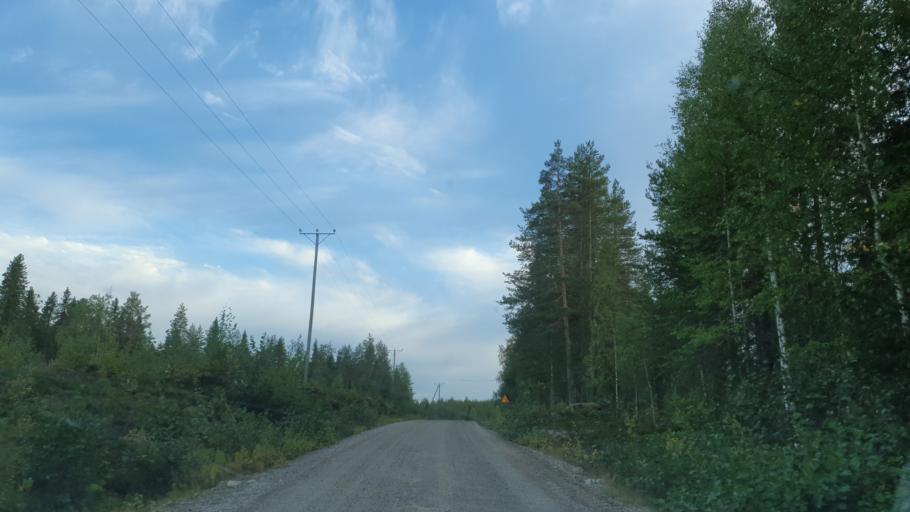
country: FI
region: Kainuu
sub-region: Kehys-Kainuu
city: Kuhmo
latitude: 64.3603
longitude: 29.5740
